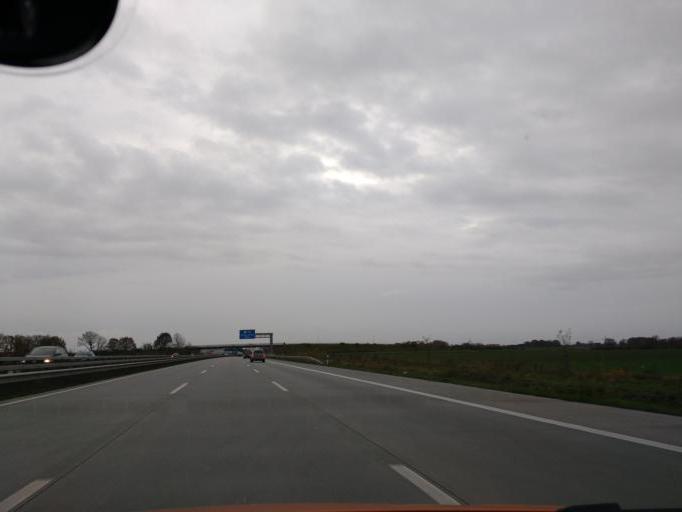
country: DE
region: Lower Saxony
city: Reessum
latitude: 53.1216
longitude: 9.2109
